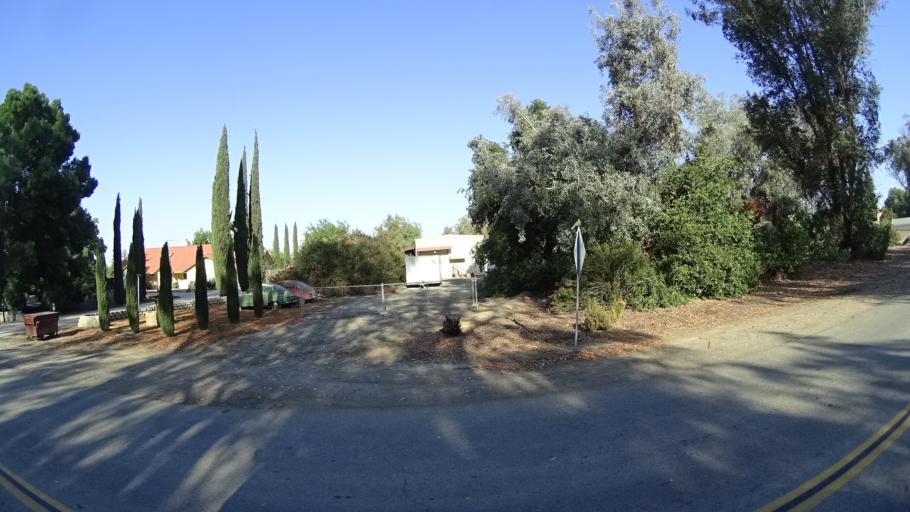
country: US
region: California
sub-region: Kings County
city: Lemoore
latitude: 36.2996
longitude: -119.7446
